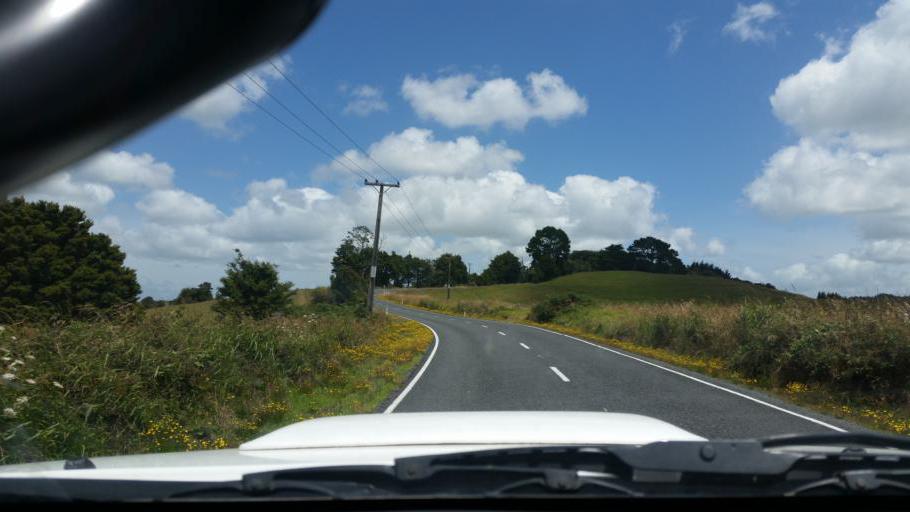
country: NZ
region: Northland
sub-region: Whangarei
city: Ruakaka
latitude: -36.0442
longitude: 174.2786
